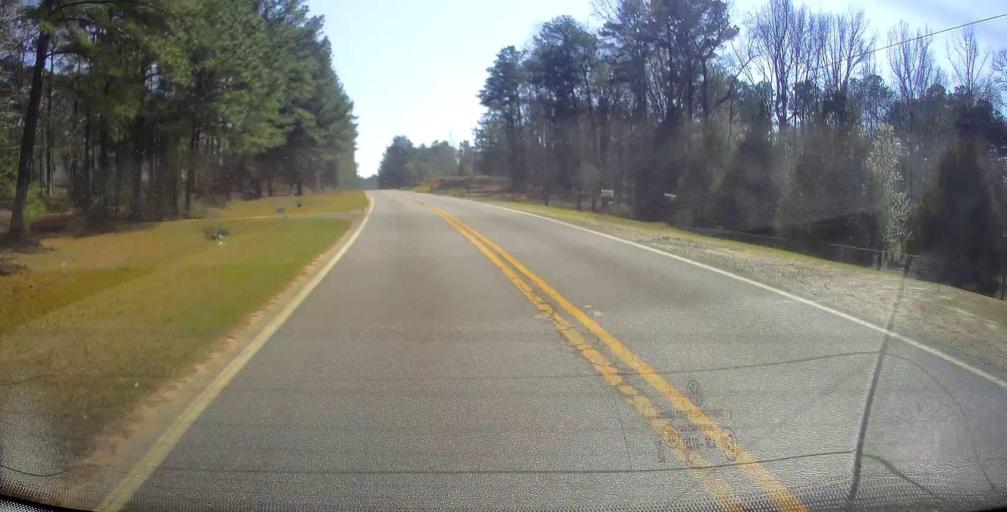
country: US
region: Georgia
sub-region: Jones County
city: Gray
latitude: 32.9321
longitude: -83.5356
